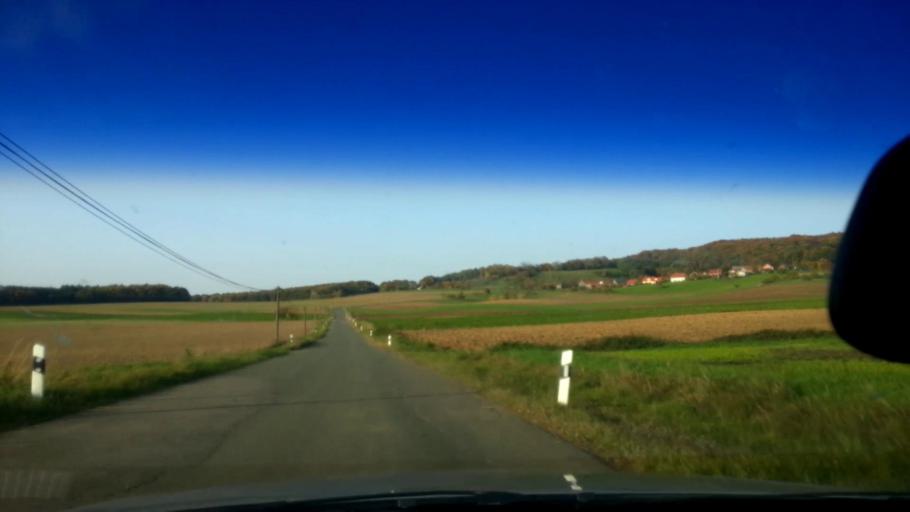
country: DE
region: Bavaria
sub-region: Upper Franconia
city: Schesslitz
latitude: 50.0092
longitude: 11.0201
